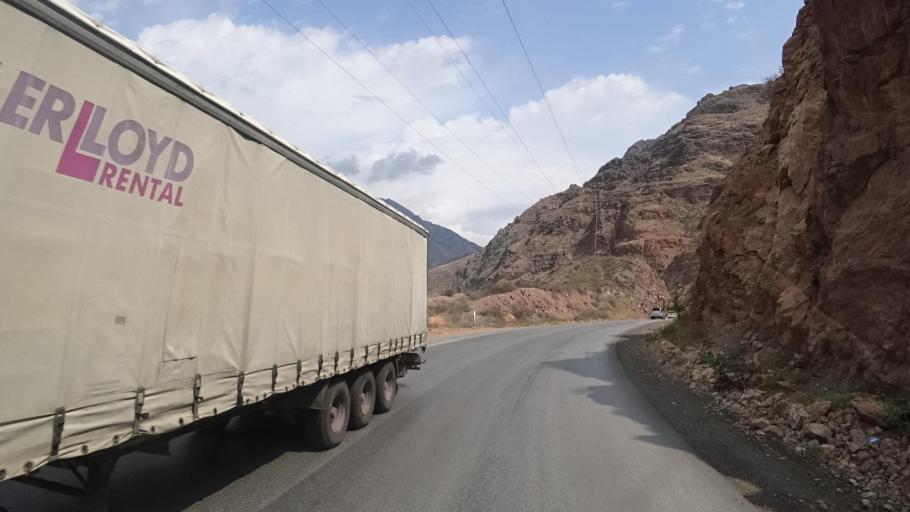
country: KG
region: Jalal-Abad
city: Tash-Kumyr
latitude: 41.5973
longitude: 72.5704
